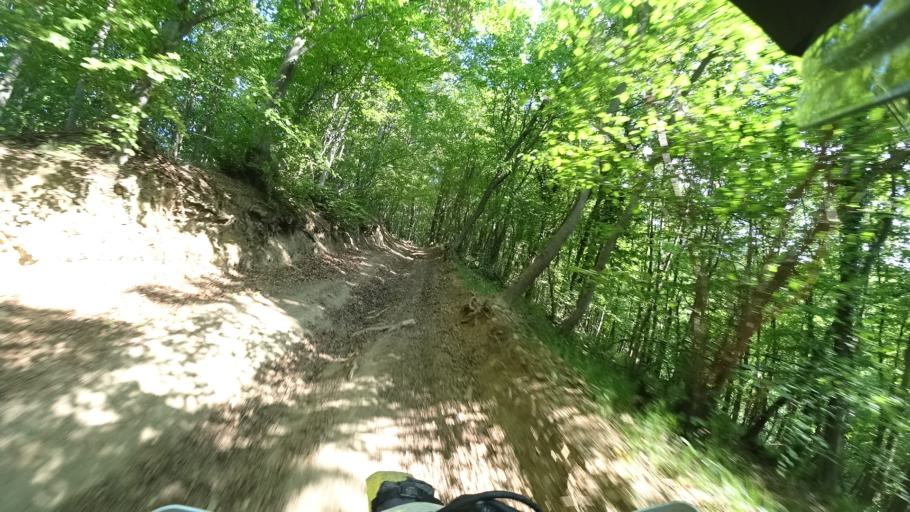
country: HR
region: Zagrebacka
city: Jablanovec
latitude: 45.8762
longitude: 15.8763
